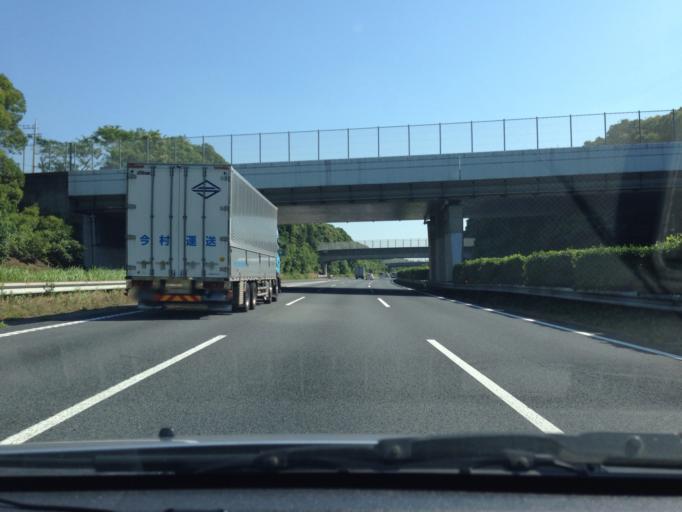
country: JP
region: Ibaraki
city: Ishioka
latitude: 36.2016
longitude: 140.2623
